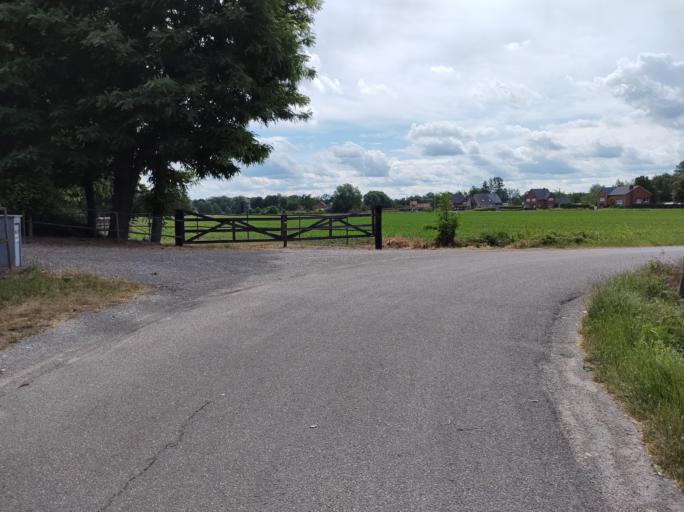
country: BE
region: Flanders
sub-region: Provincie Limburg
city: Diepenbeek
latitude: 50.9286
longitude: 5.4082
